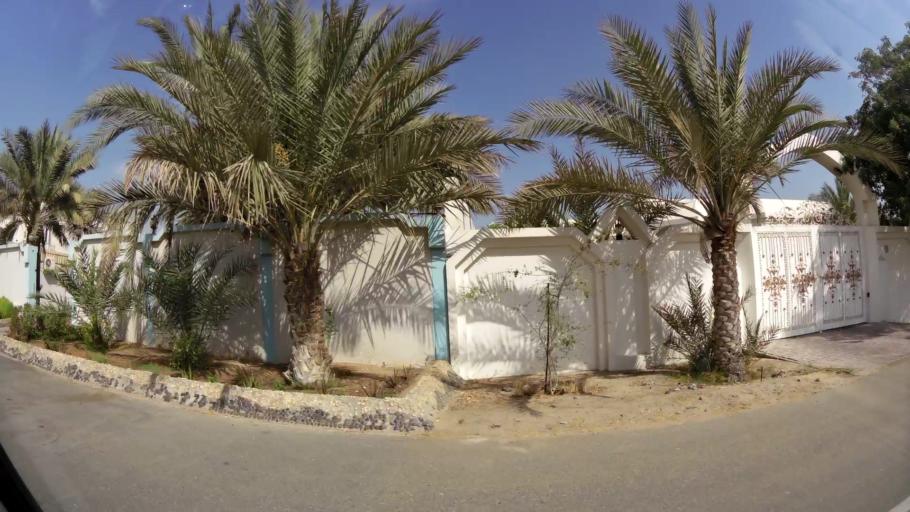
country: AE
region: Ash Shariqah
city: Sharjah
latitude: 25.2748
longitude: 55.4021
